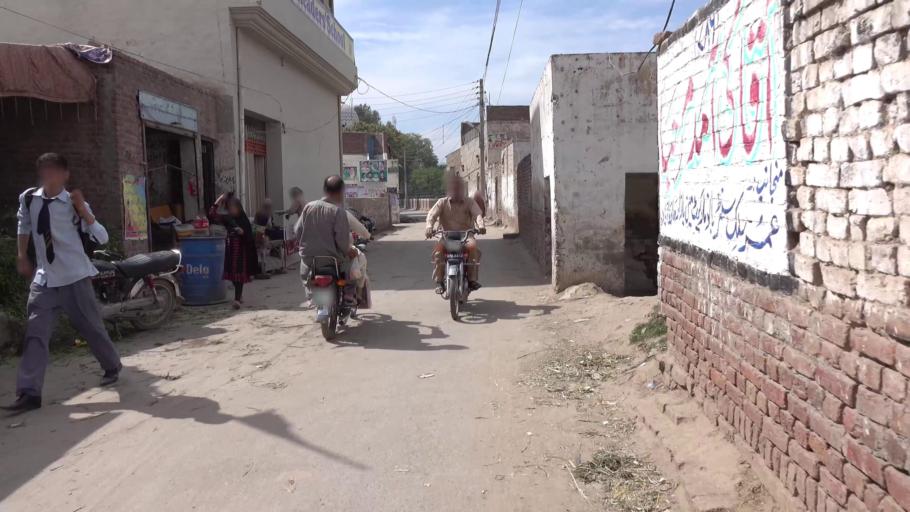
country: PK
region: Punjab
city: Hafizabad
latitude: 32.0662
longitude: 73.6853
